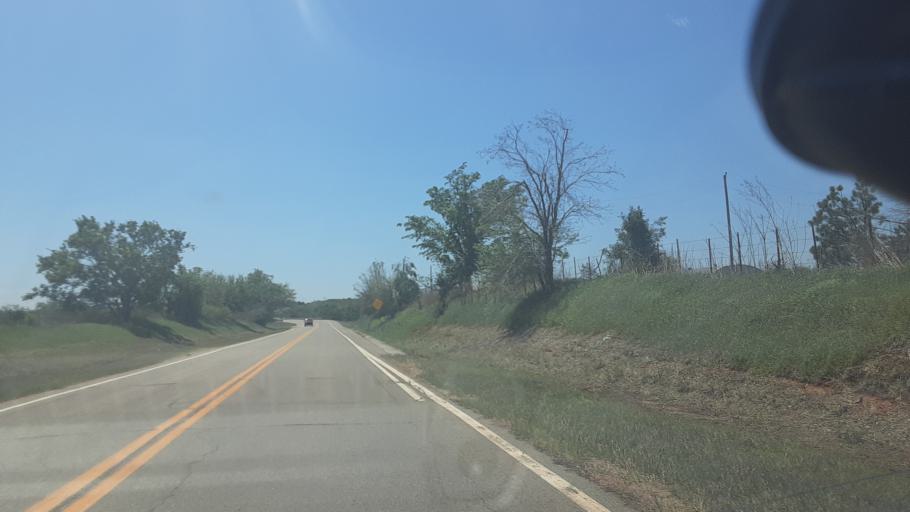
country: US
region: Oklahoma
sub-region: Logan County
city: Guthrie
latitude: 36.0552
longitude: -97.4082
